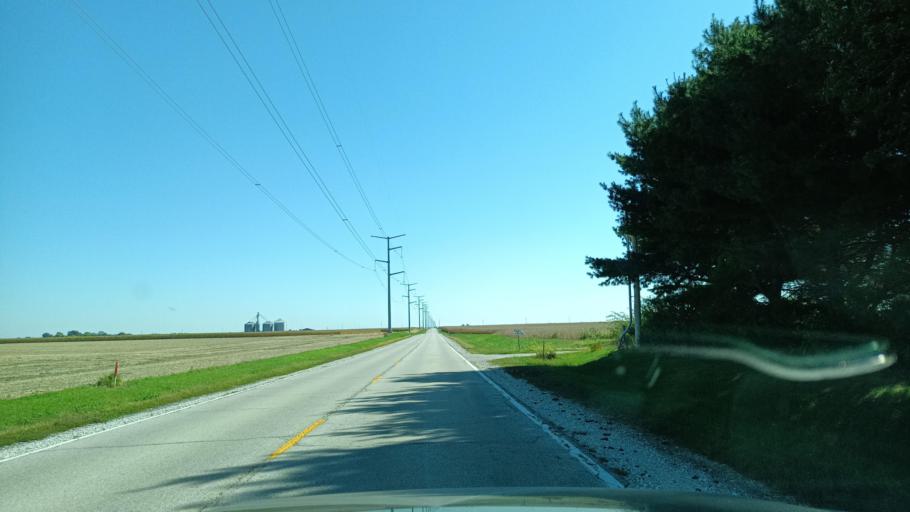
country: US
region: Illinois
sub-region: Peoria County
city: Elmwood
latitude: 40.9024
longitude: -90.0315
